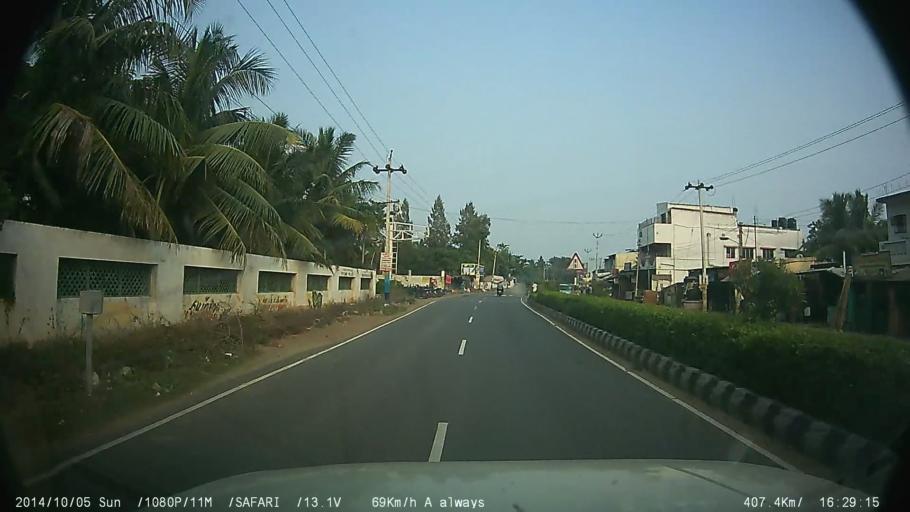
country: IN
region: Tamil Nadu
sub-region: Kancheepuram
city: Vengavasal
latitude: 12.7926
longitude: 80.2162
